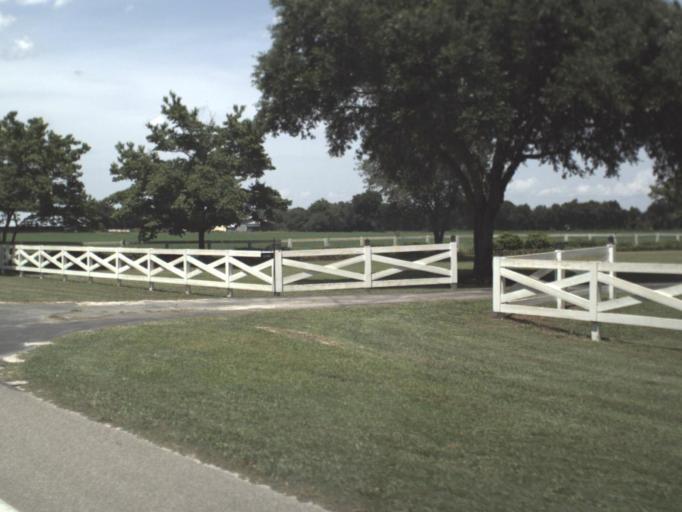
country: US
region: Florida
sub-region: Gilchrist County
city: Trenton
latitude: 29.7062
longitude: -82.8575
